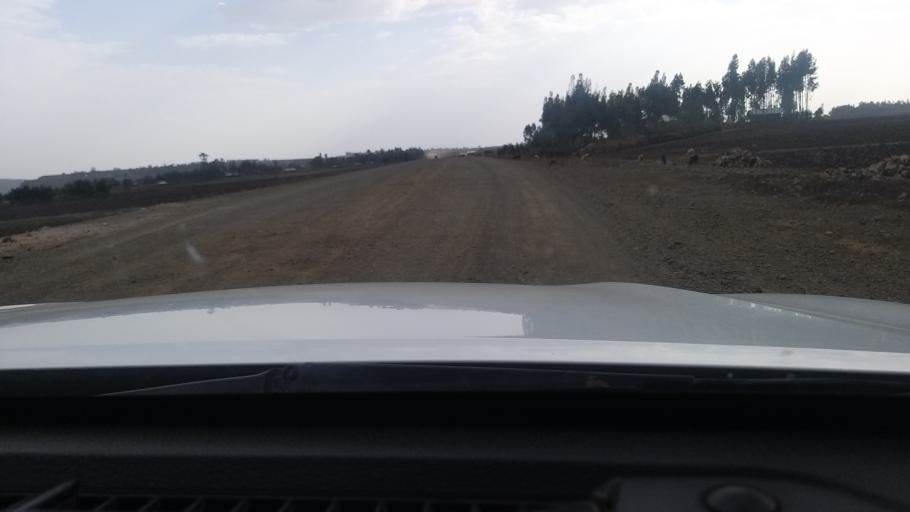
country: ET
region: Amhara
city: Were Ilu
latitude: 10.4531
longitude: 39.2103
